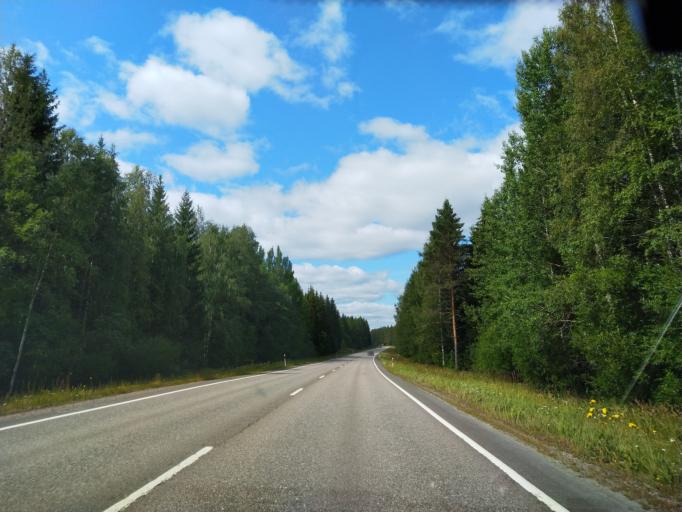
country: FI
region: Haeme
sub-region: Haemeenlinna
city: Renko
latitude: 60.7672
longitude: 24.2427
